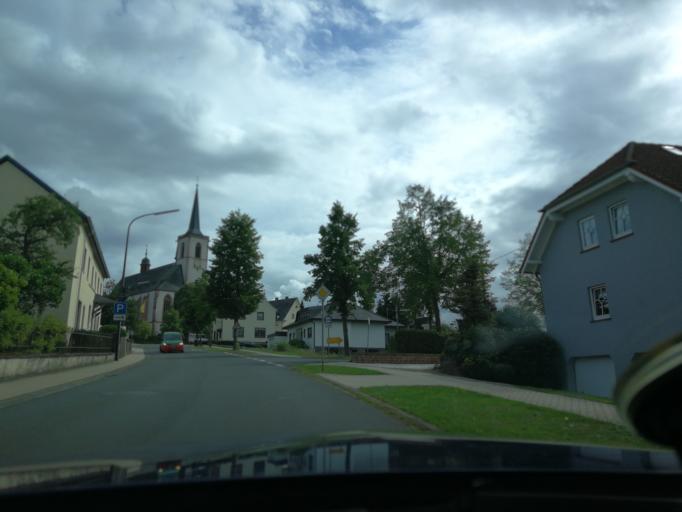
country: DE
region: Rheinland-Pfalz
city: Klausen
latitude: 49.9067
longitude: 6.8828
